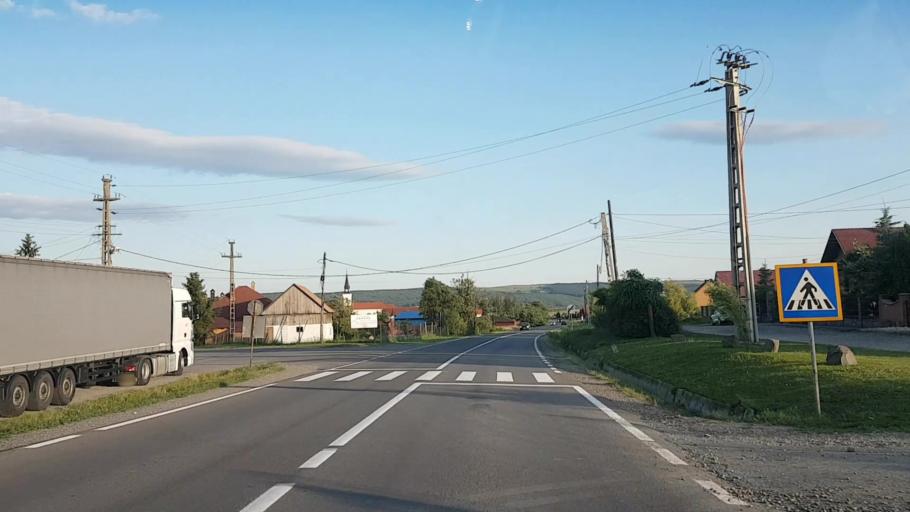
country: RO
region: Harghita
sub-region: Comuna Lupeni
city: Lupeni
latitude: 46.3816
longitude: 25.2192
